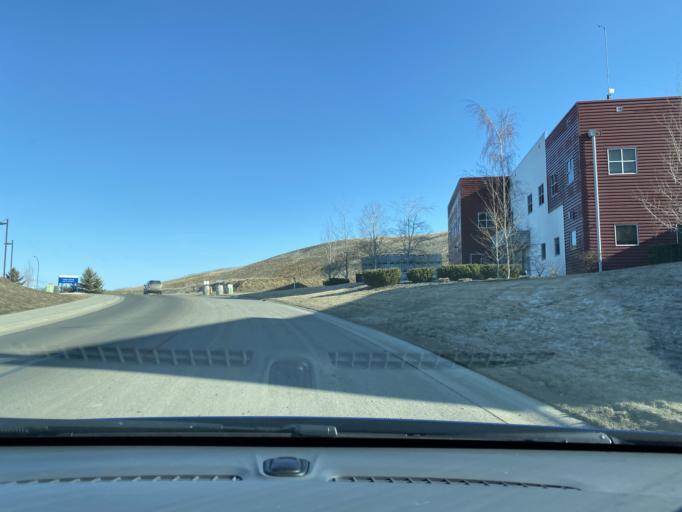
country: US
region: Washington
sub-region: Whitman County
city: Pullman
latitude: 46.7511
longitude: -117.1573
